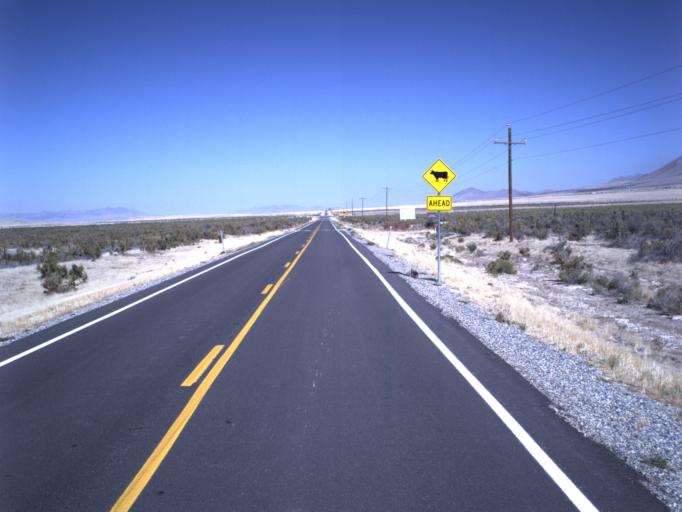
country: US
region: Utah
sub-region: Tooele County
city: Grantsville
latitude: 40.3452
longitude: -112.7451
